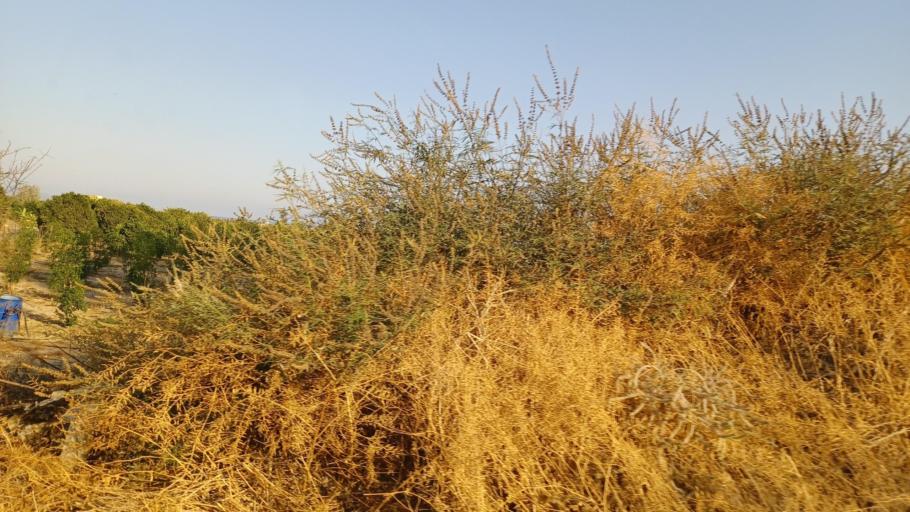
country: CY
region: Pafos
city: Polis
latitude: 35.0594
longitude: 32.4651
